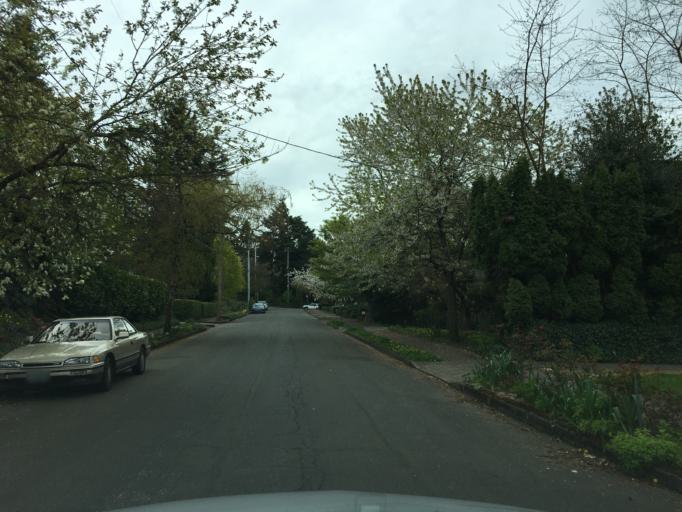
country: US
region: Oregon
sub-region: Multnomah County
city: Lents
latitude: 45.5205
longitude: -122.5996
